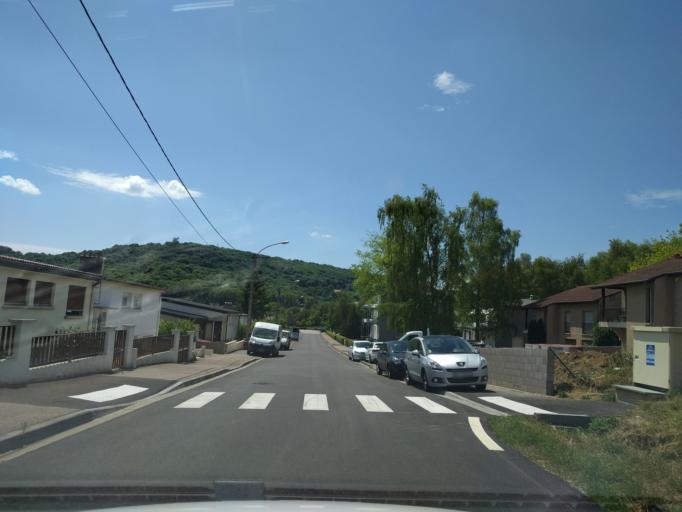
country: FR
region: Lorraine
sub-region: Departement de la Moselle
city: Le Ban Saint-Martin
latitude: 49.1314
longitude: 6.1413
